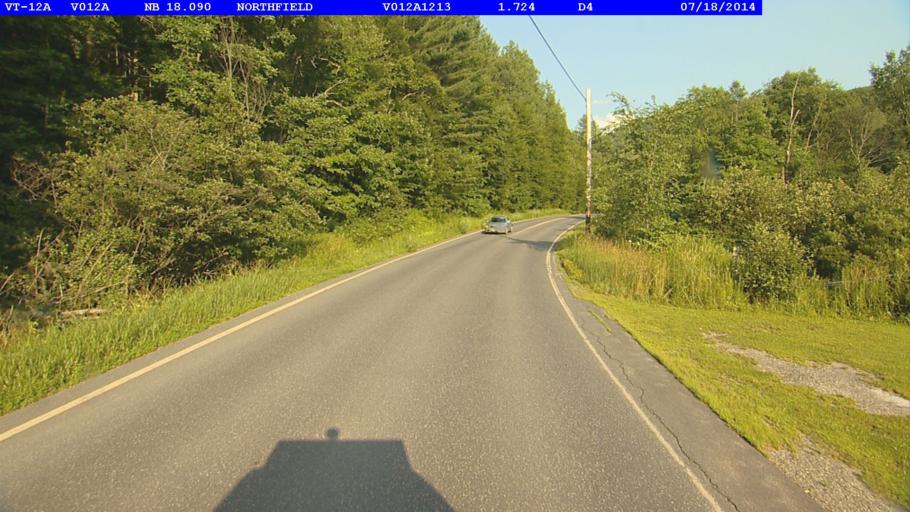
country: US
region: Vermont
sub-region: Washington County
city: Northfield
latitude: 44.1127
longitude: -72.6950
